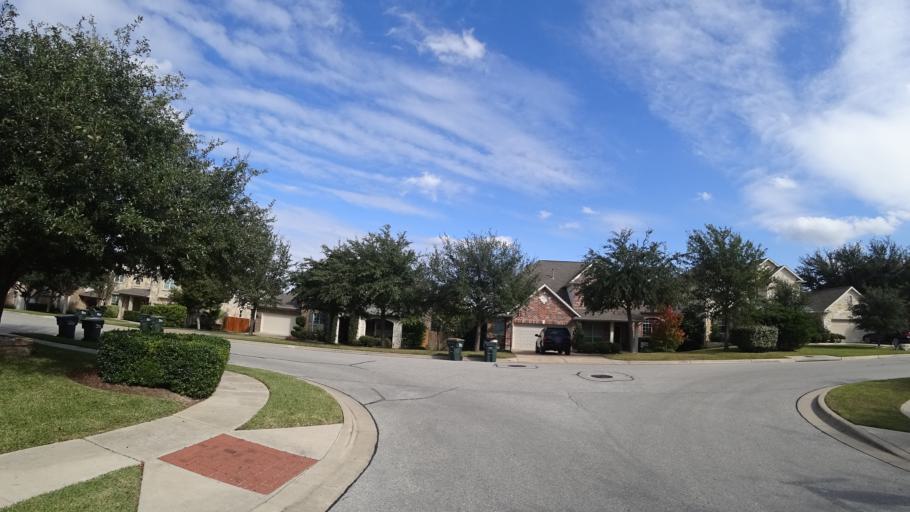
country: US
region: Texas
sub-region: Travis County
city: Hudson Bend
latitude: 30.3700
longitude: -97.9034
